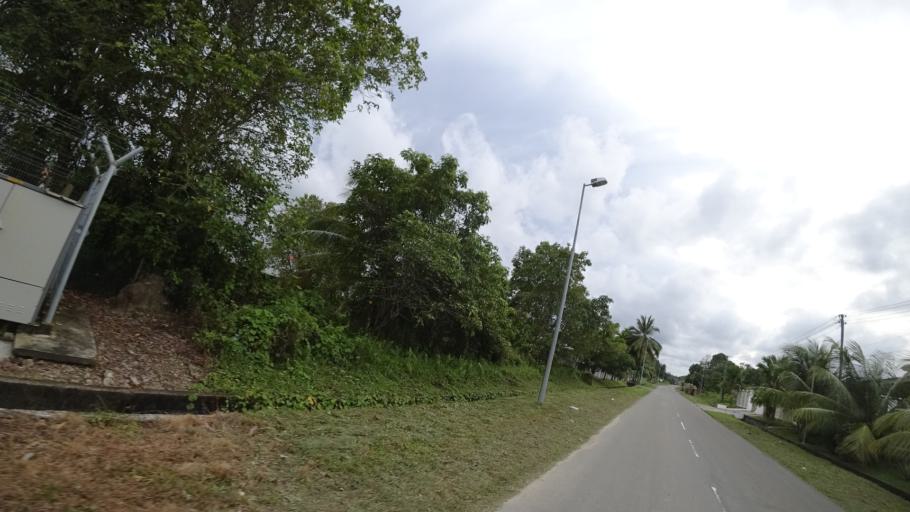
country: BN
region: Brunei and Muara
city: Bandar Seri Begawan
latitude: 4.8550
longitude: 114.8522
